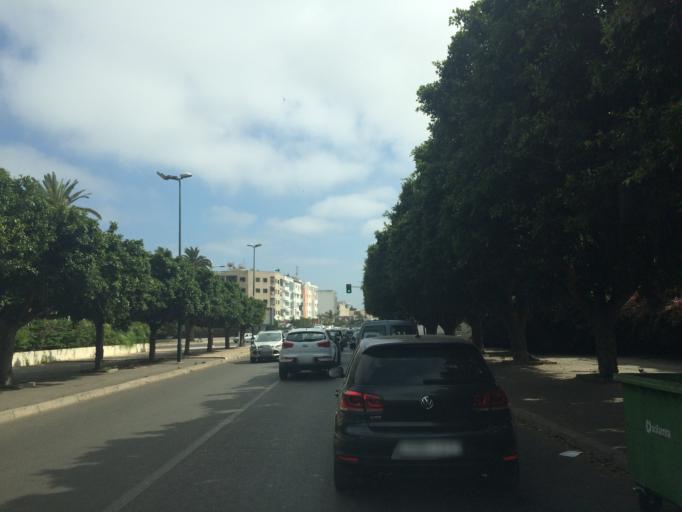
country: MA
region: Rabat-Sale-Zemmour-Zaer
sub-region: Rabat
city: Rabat
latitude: 34.0101
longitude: -6.8515
